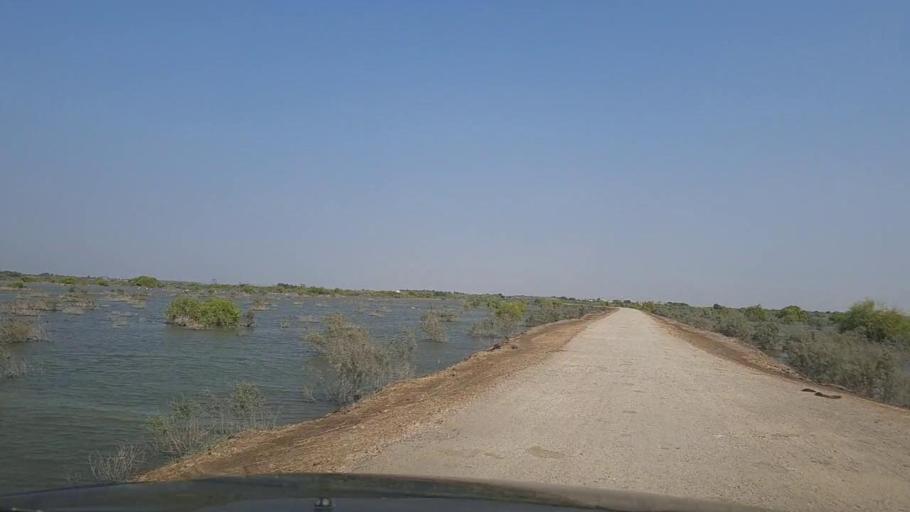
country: PK
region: Sindh
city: Thatta
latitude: 24.6411
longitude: 67.8145
